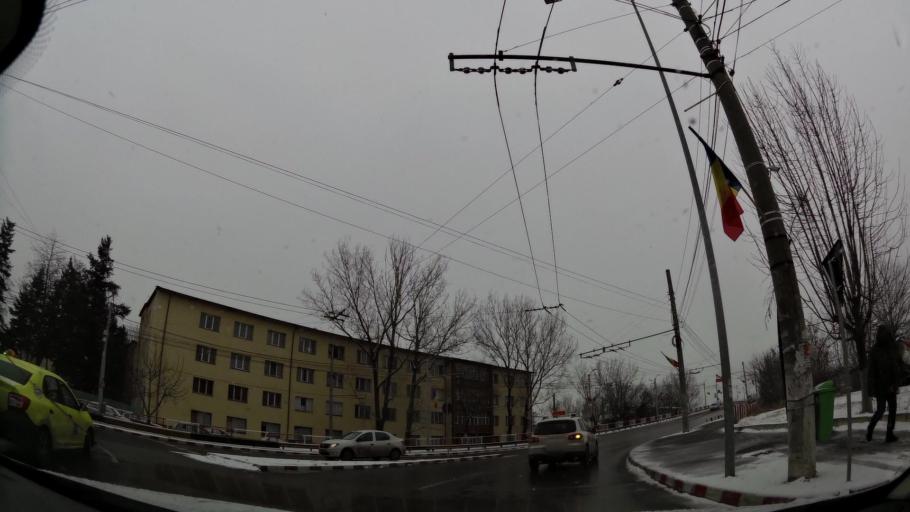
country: RO
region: Dambovita
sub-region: Municipiul Targoviste
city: Targoviste
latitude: 44.9192
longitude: 25.4527
